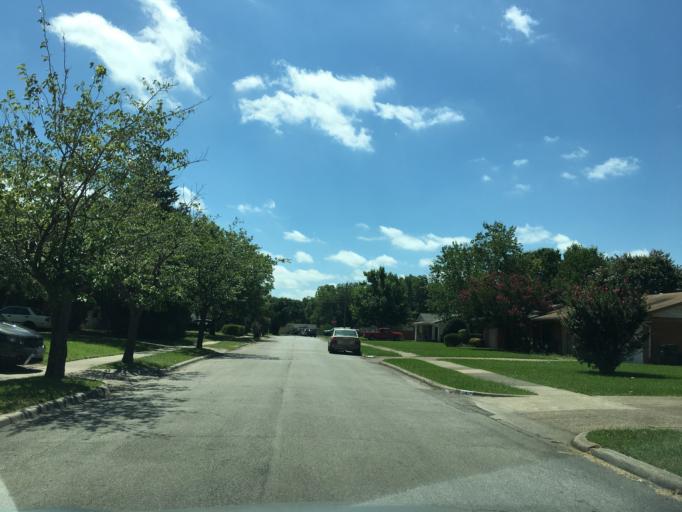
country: US
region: Texas
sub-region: Dallas County
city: Garland
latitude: 32.8361
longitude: -96.6542
